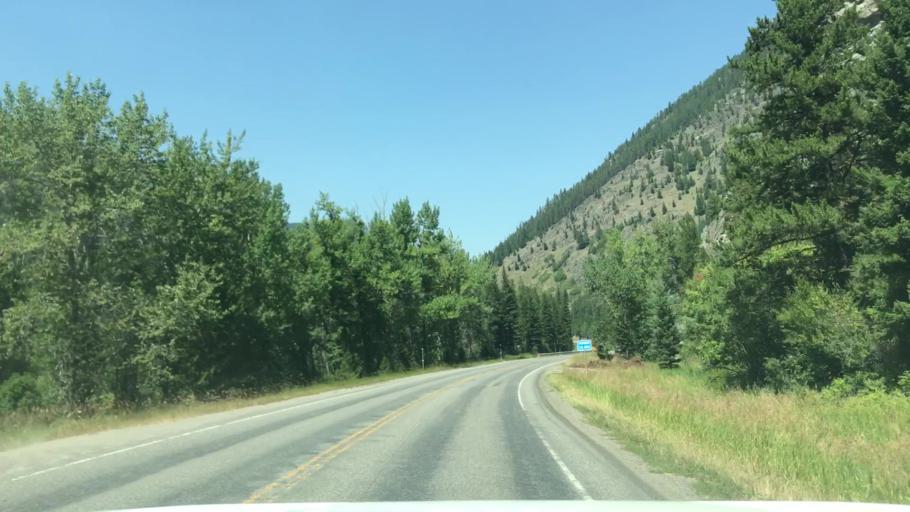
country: US
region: Montana
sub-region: Gallatin County
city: Big Sky
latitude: 45.4004
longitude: -111.2172
